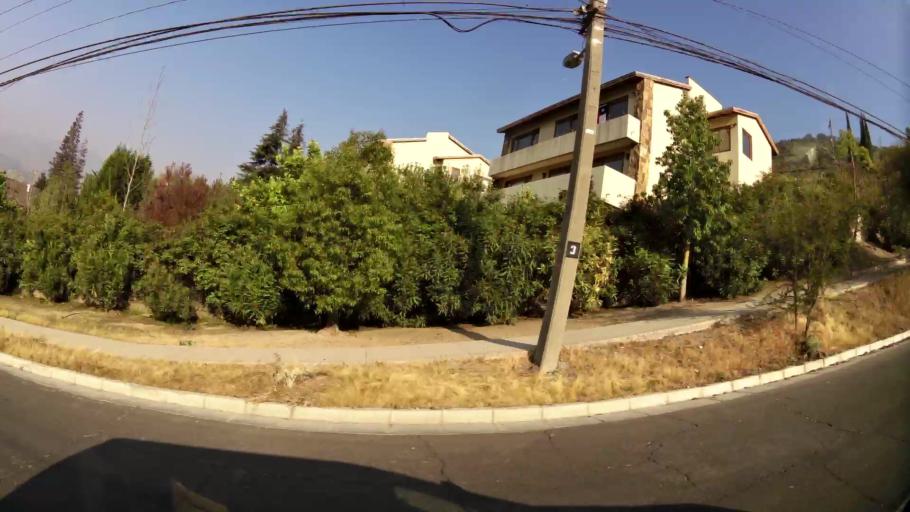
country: CL
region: Santiago Metropolitan
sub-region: Provincia de Santiago
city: Villa Presidente Frei, Nunoa, Santiago, Chile
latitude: -33.3674
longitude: -70.5297
